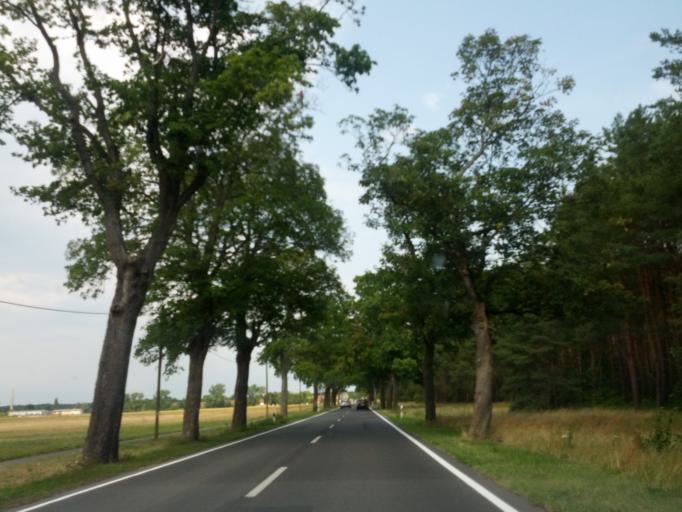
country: DE
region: Brandenburg
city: Nauen
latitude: 52.6755
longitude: 12.9320
